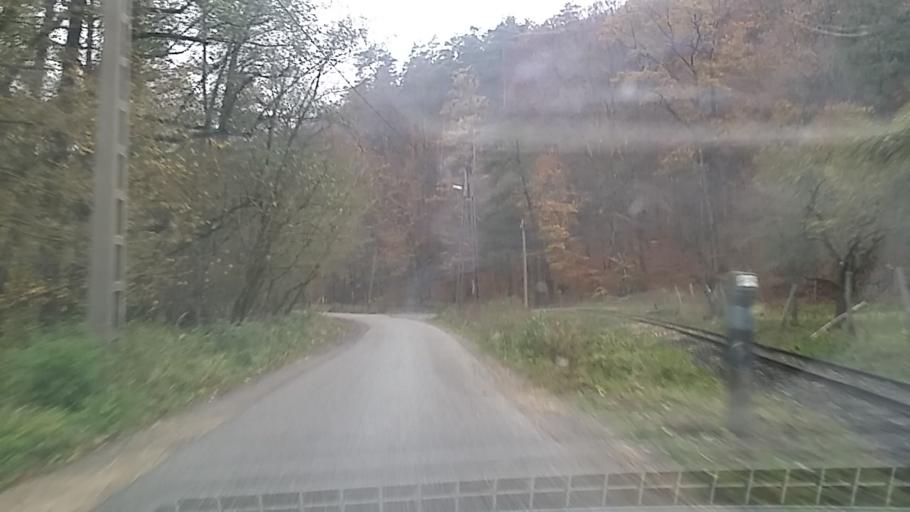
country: HU
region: Borsod-Abauj-Zemplen
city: Tolcsva
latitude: 48.4472
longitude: 21.4625
